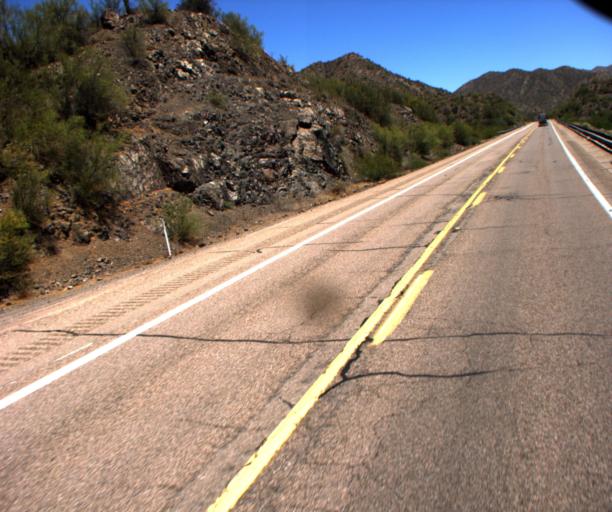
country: US
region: Arizona
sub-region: Pinal County
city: Kearny
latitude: 33.0191
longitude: -110.7441
